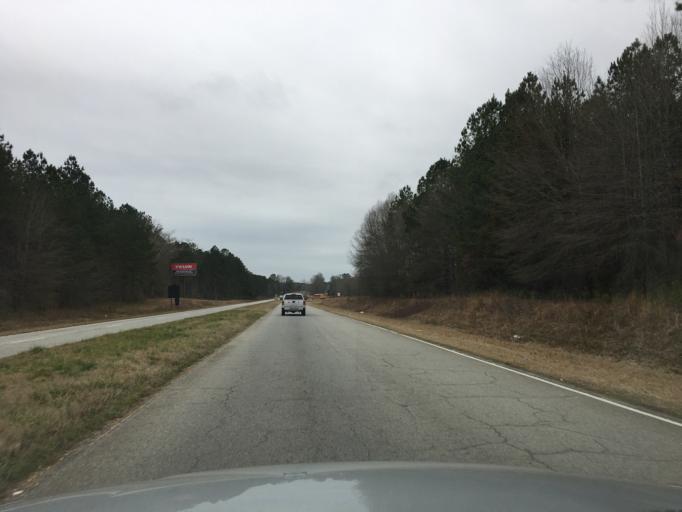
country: US
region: South Carolina
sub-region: Greenwood County
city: Greenwood
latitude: 34.1516
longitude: -82.1401
